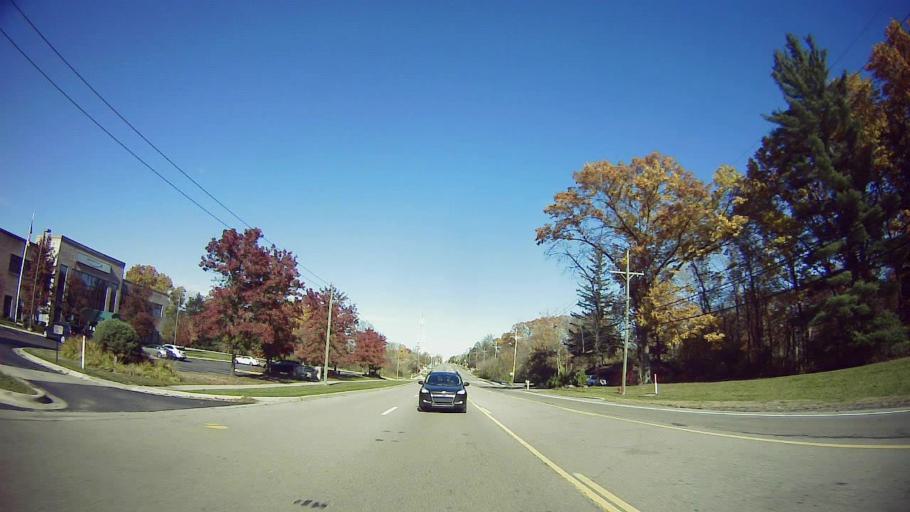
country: US
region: Michigan
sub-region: Oakland County
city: Southfield
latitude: 42.4665
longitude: -83.2605
